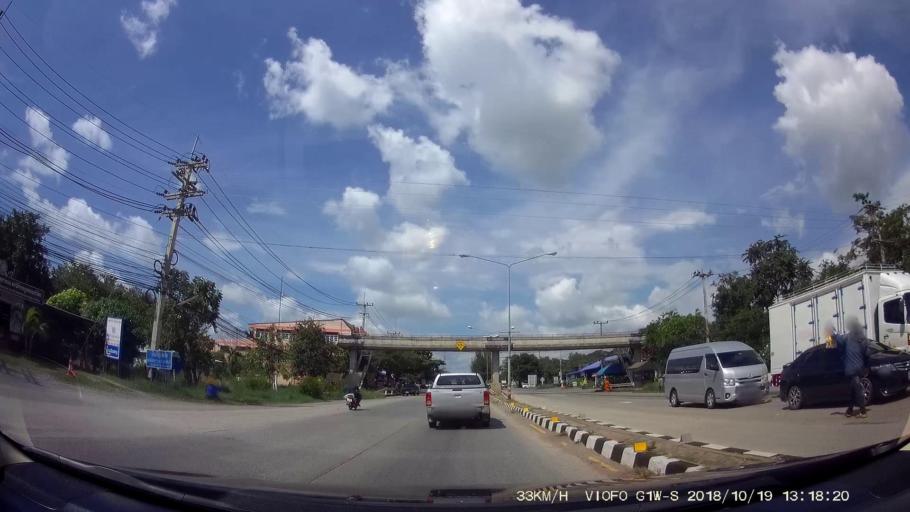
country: TH
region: Chaiyaphum
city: Chatturat
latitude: 15.4149
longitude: 101.8333
